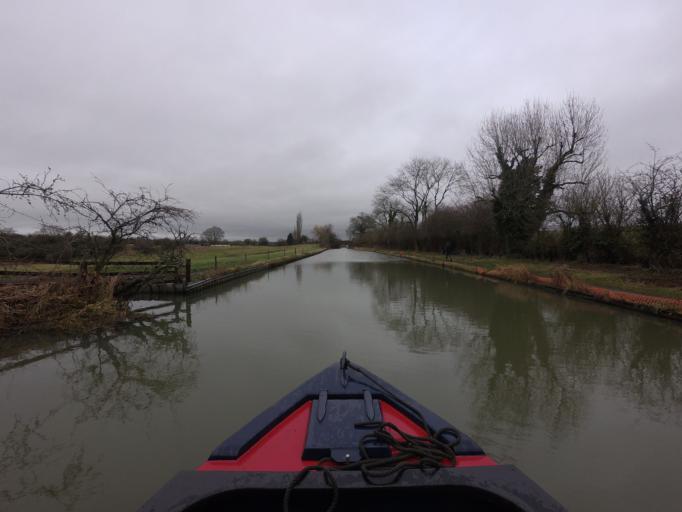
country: GB
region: England
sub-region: Northamptonshire
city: Long Buckby
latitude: 52.2846
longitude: -1.1205
